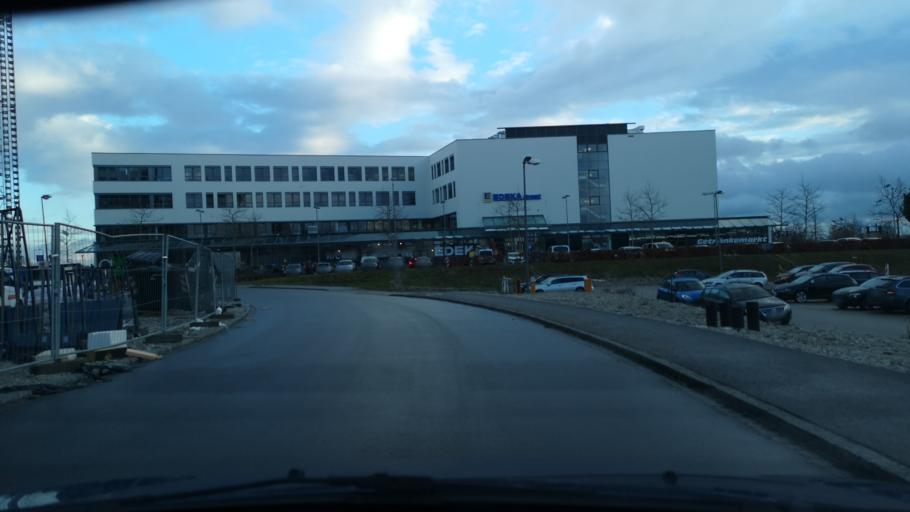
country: DE
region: Bavaria
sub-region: Upper Bavaria
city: Garching bei Munchen
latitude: 48.2504
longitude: 11.6328
